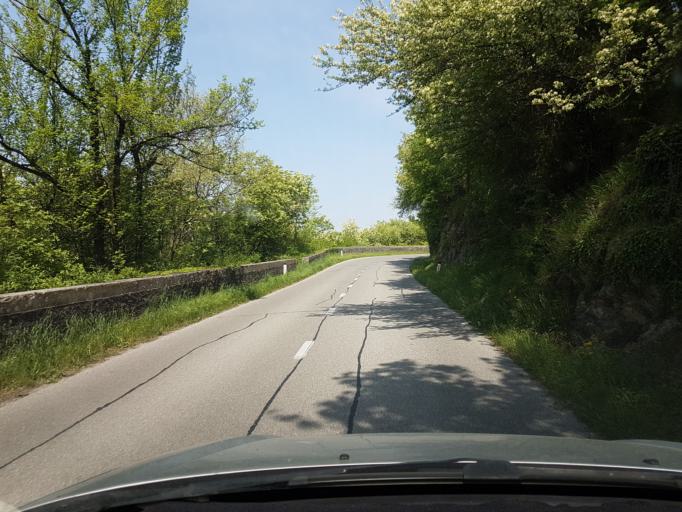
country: SI
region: Komen
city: Komen
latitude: 45.7990
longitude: 13.7104
